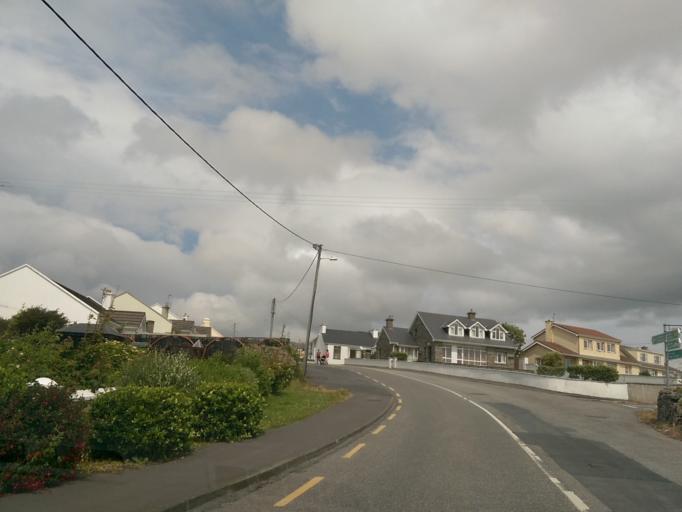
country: IE
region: Munster
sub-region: An Clar
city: Kilrush
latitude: 52.6836
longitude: -9.6429
